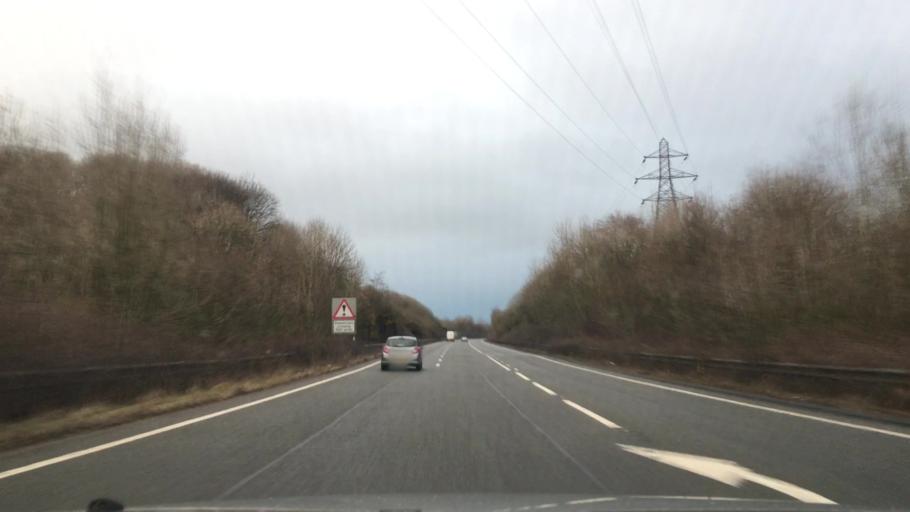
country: GB
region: England
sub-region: Cumbria
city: Askam in Furness
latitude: 54.1617
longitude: -3.2002
